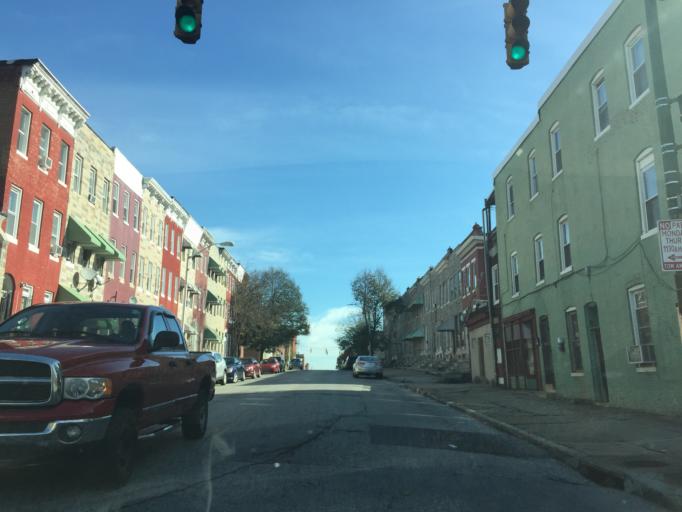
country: US
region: Maryland
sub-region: City of Baltimore
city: Baltimore
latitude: 39.2920
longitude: -76.6471
